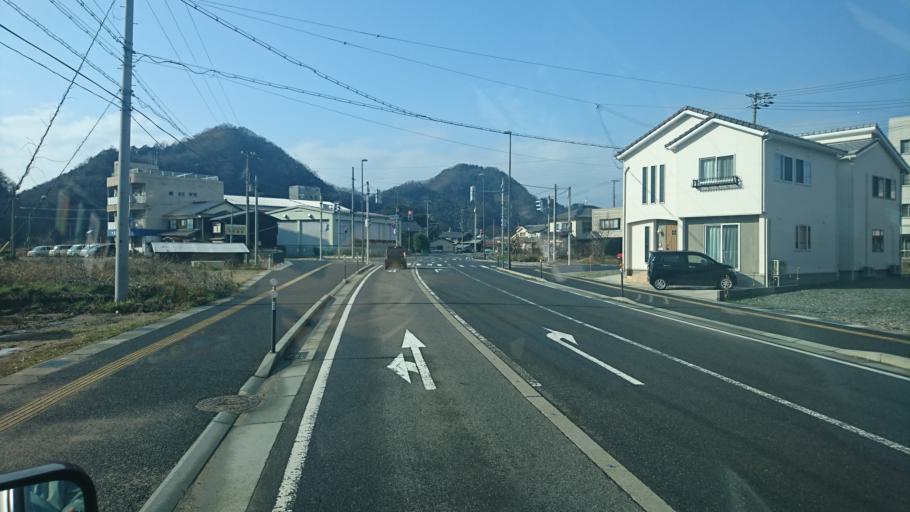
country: JP
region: Tottori
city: Tottori
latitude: 35.6230
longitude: 134.4469
